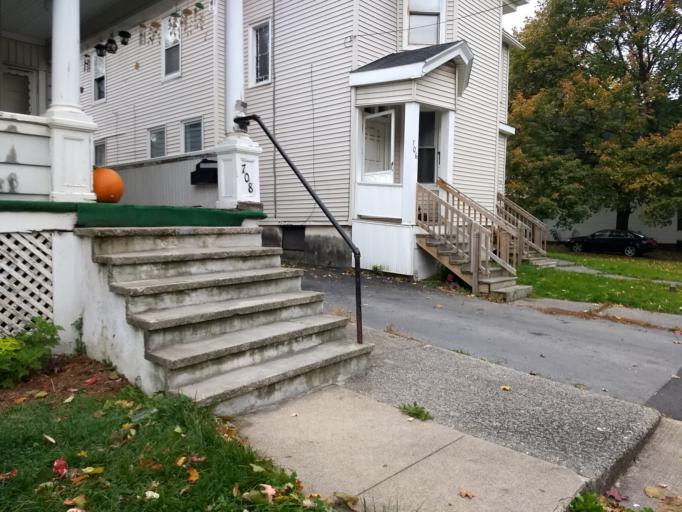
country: US
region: New York
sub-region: Onondaga County
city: Galeville
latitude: 43.0738
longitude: -76.1581
